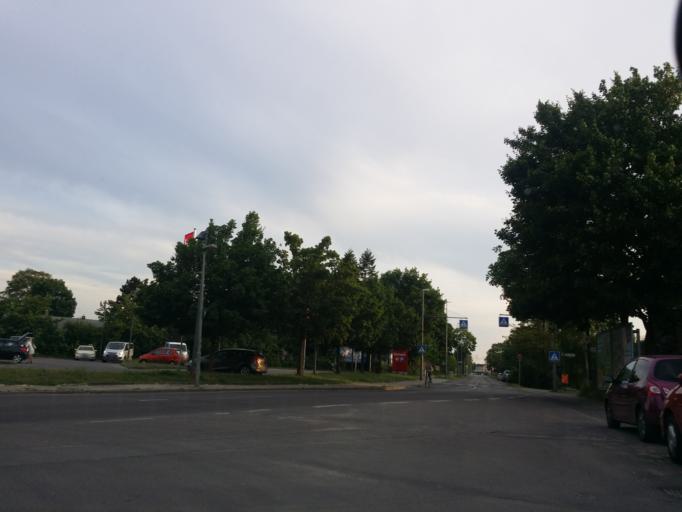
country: DE
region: Berlin
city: Altglienicke
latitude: 52.4185
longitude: 13.5363
